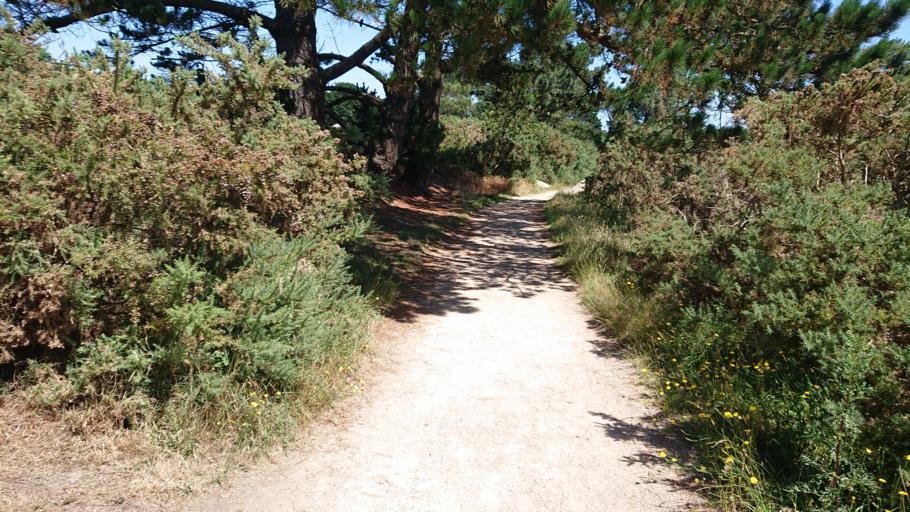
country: FR
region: Brittany
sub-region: Departement des Cotes-d'Armor
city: Tregastel
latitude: 48.8307
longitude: -3.4790
